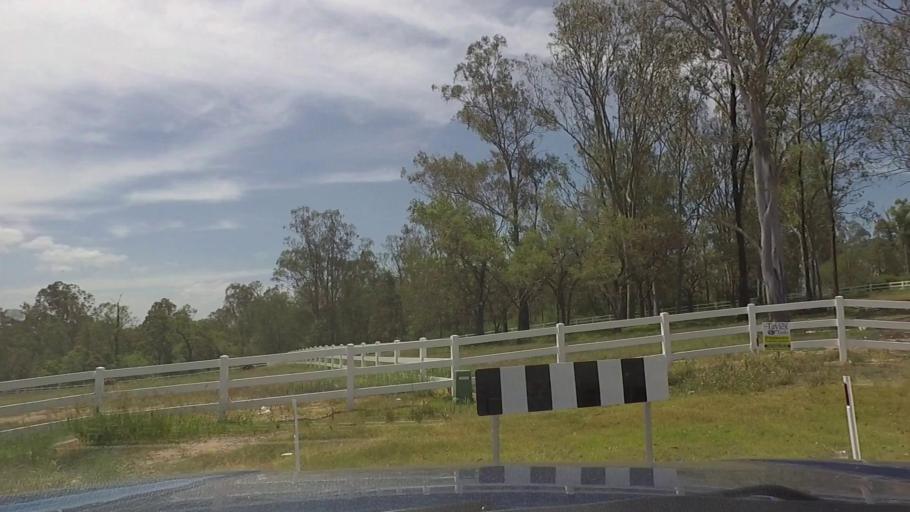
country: AU
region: Queensland
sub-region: Logan
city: North Maclean
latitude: -27.7759
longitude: 153.0349
